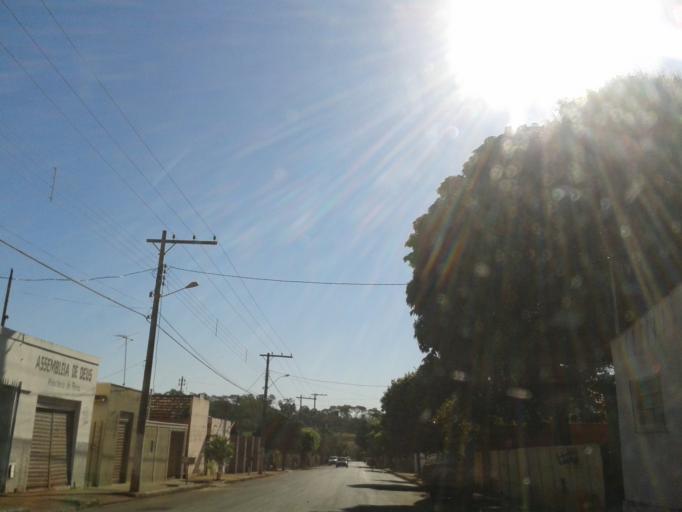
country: BR
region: Minas Gerais
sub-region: Capinopolis
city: Capinopolis
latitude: -18.6796
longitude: -49.5699
